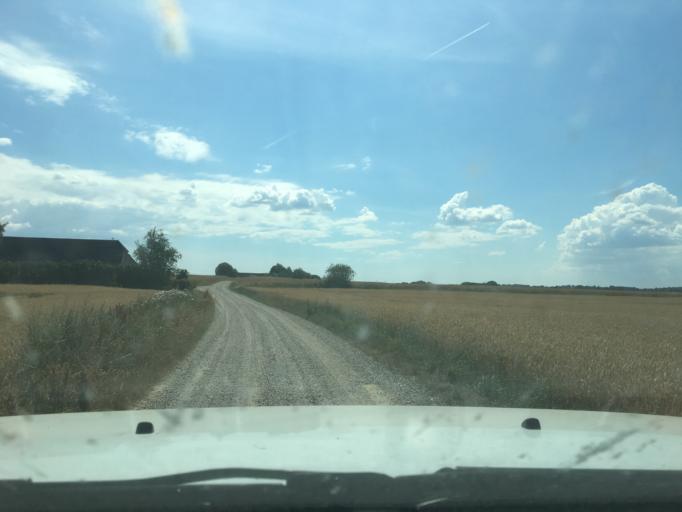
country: DK
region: Central Jutland
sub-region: Randers Kommune
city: Assentoft
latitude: 56.3493
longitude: 10.1867
